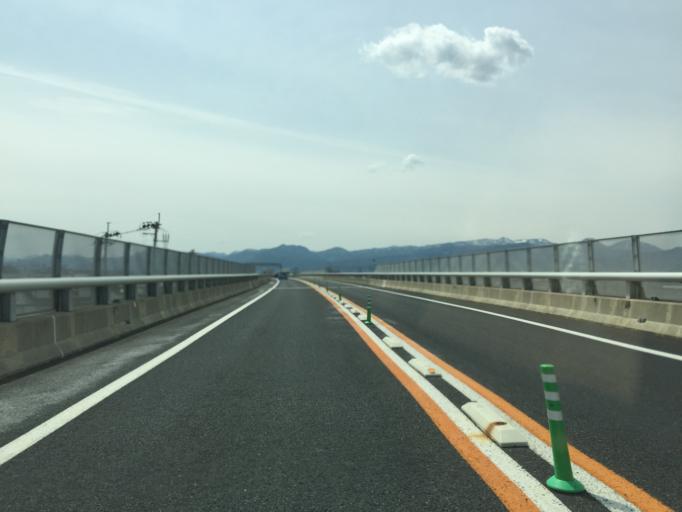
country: JP
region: Yamagata
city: Sagae
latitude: 38.2976
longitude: 140.3033
